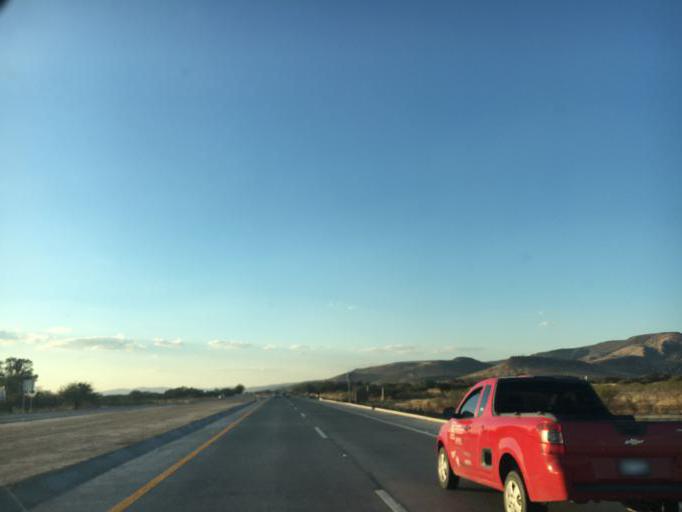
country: MX
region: Guanajuato
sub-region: Leon
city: Ladrilleras del Refugio
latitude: 21.0884
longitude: -101.5588
